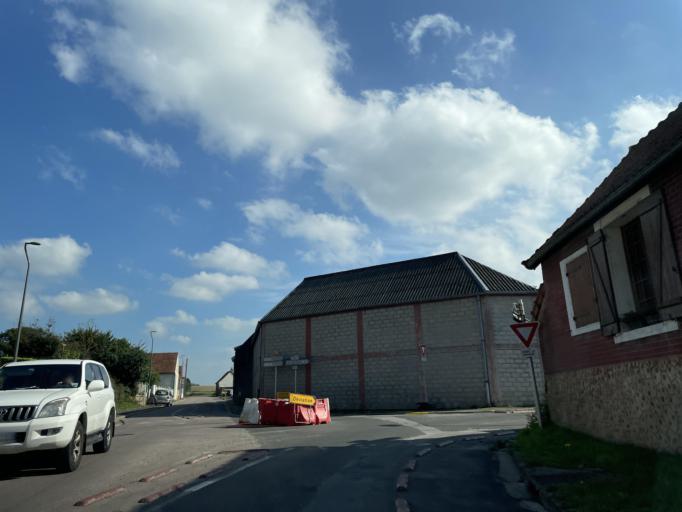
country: FR
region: Haute-Normandie
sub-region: Departement de la Seine-Maritime
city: Criel-sur-Mer
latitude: 50.0389
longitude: 1.3418
